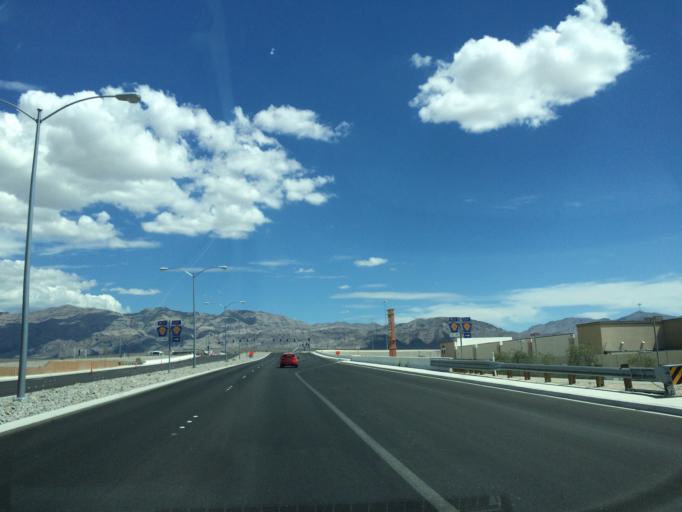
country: US
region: Nevada
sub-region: Clark County
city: Nellis Air Force Base
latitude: 36.2881
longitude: -115.1349
